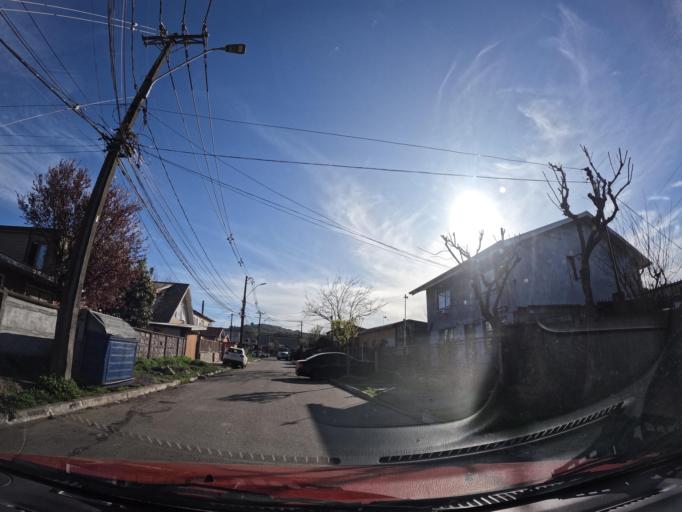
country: CL
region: Biobio
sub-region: Provincia de Concepcion
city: Talcahuano
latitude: -36.7697
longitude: -73.0824
